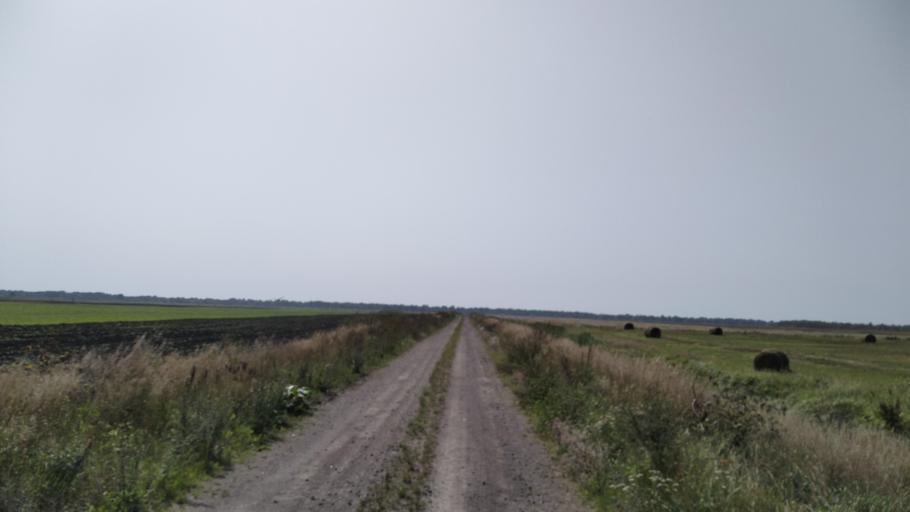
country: BY
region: Brest
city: Davyd-Haradok
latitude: 51.9844
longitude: 27.1638
